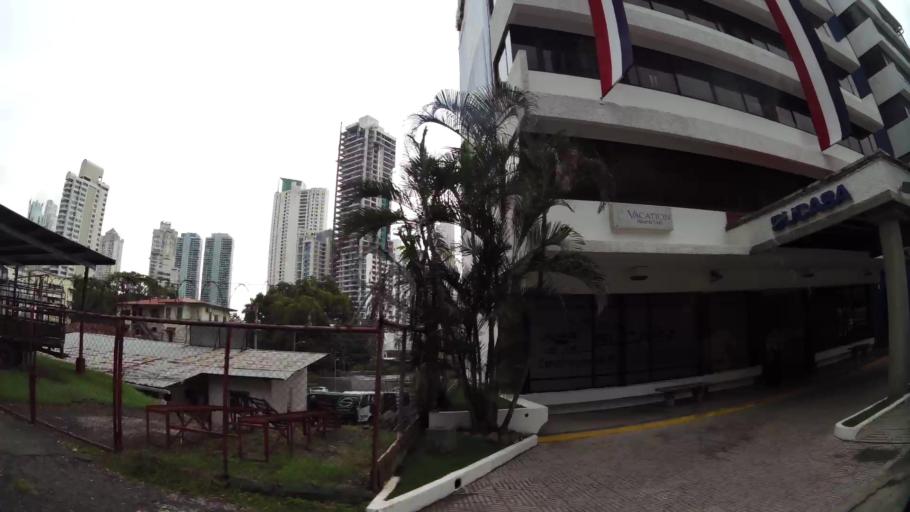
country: PA
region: Panama
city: Panama
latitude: 8.9787
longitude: -79.5313
